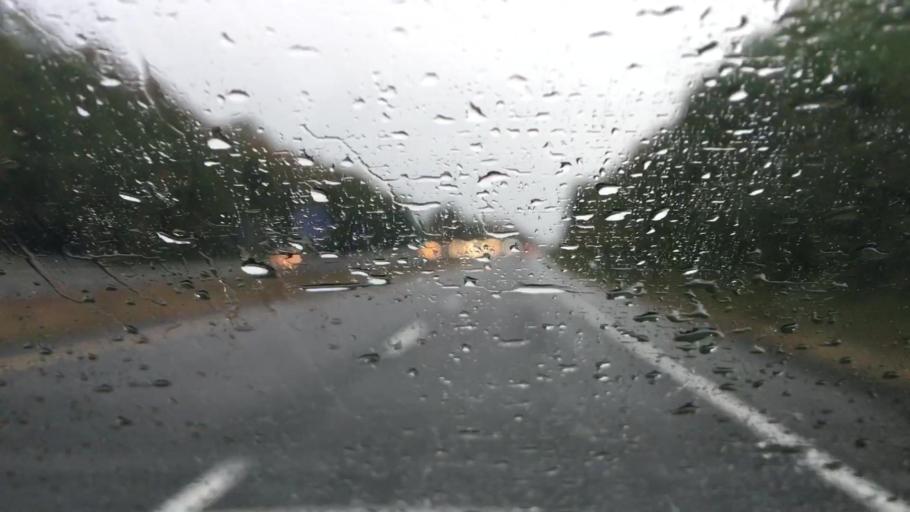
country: US
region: Maine
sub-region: Cumberland County
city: Falmouth Foreside
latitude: 43.7427
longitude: -70.2237
